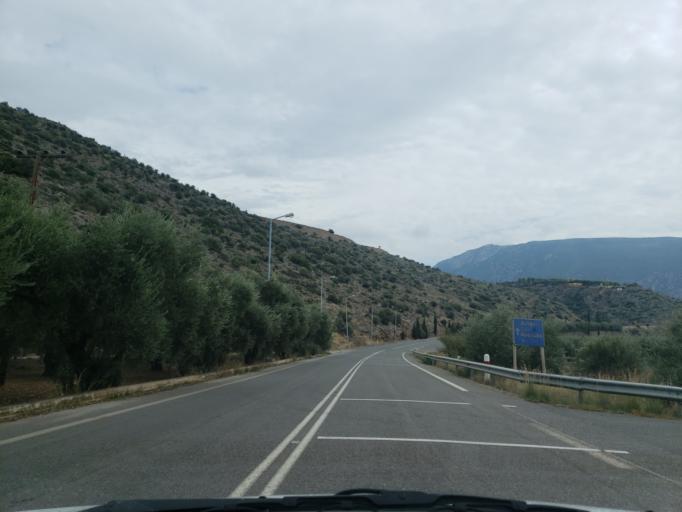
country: GR
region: Central Greece
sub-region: Nomos Fokidos
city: Delphi
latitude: 38.4776
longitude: 22.4510
